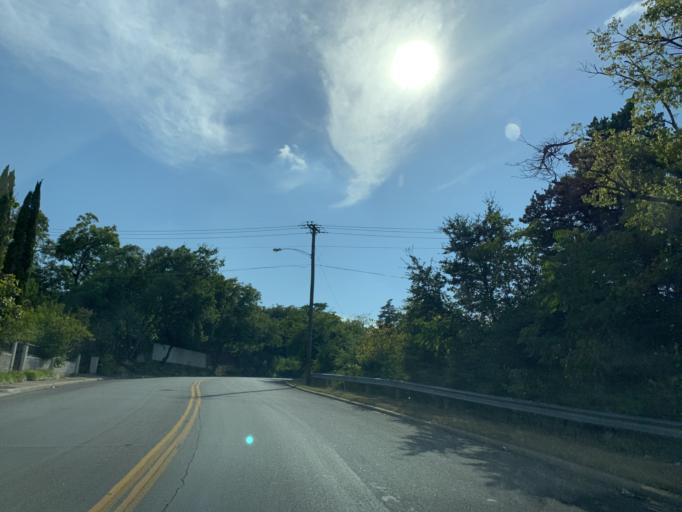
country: US
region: Texas
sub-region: Dallas County
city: Cockrell Hill
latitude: 32.7353
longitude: -96.8356
